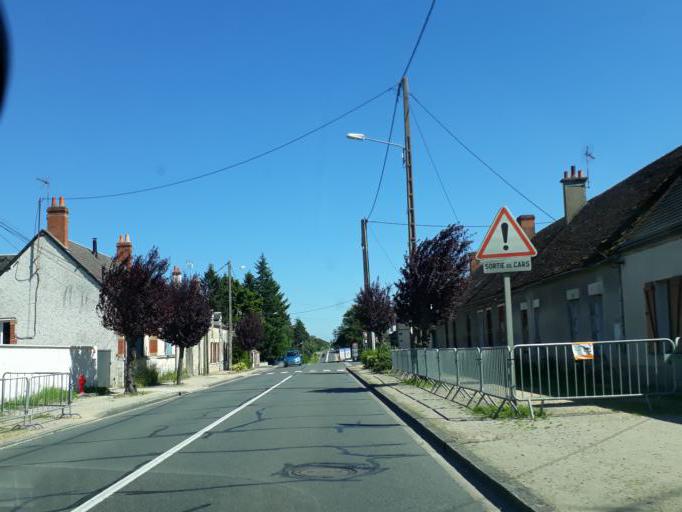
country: FR
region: Centre
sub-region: Departement du Loiret
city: Bray-en-Val
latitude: 47.8107
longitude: 2.4074
